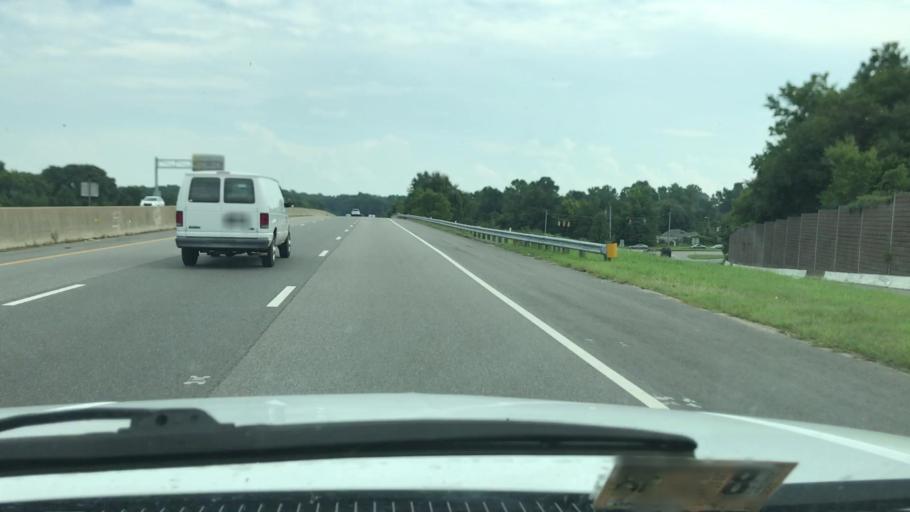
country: US
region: Virginia
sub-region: Chesterfield County
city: Bon Air
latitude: 37.4803
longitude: -77.5161
